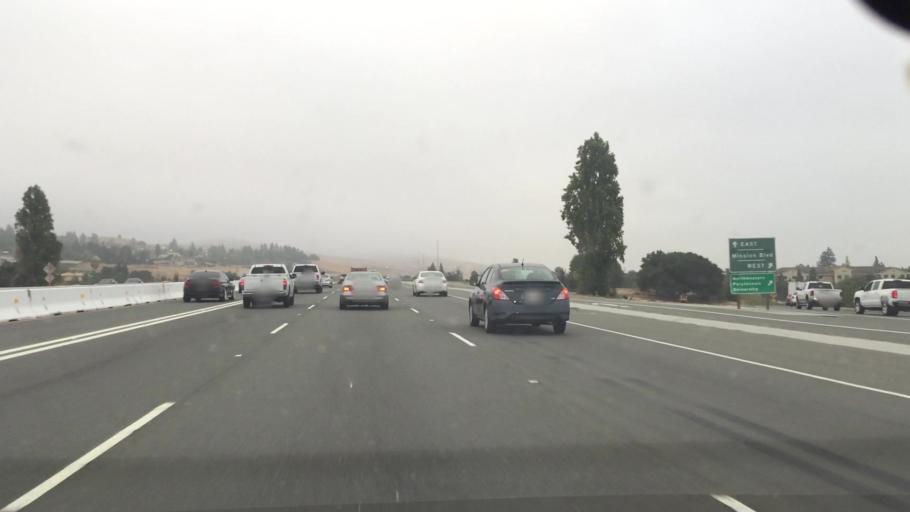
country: US
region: California
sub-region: Santa Clara County
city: Milpitas
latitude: 37.4976
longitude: -121.9261
